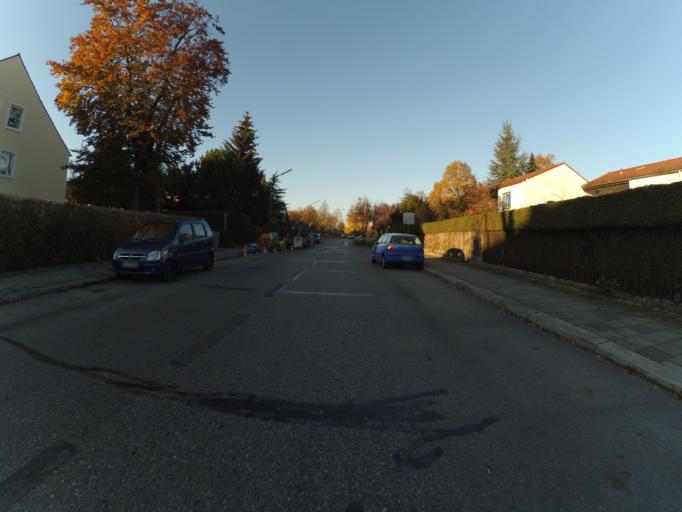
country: DE
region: Bavaria
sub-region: Upper Bavaria
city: Oberschleissheim
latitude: 48.2025
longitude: 11.5396
